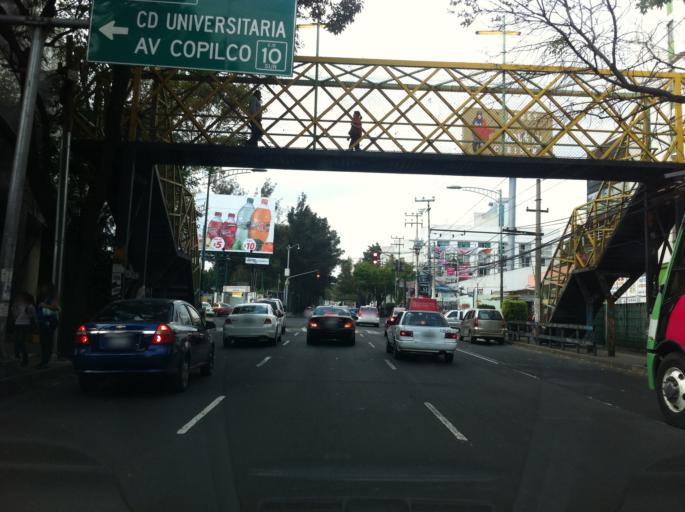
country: MX
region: Mexico City
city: Coyoacan
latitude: 19.3379
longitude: -99.1858
